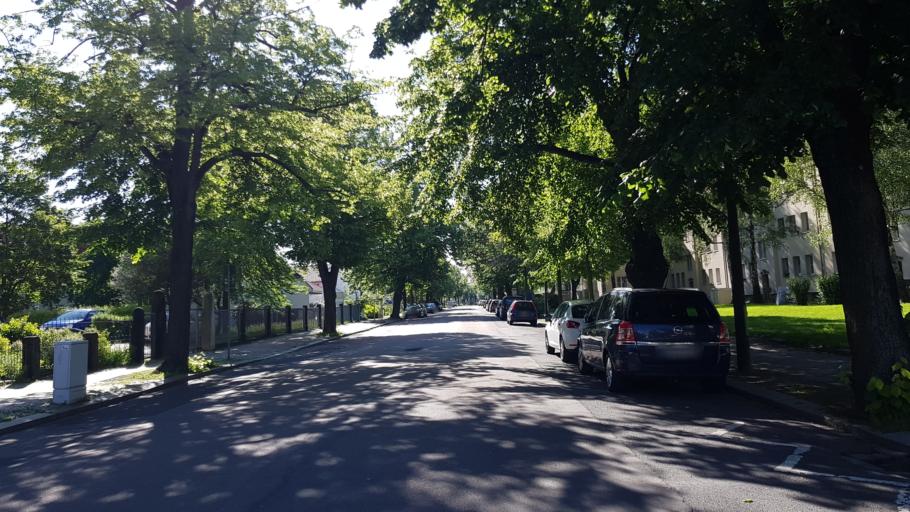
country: DE
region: Saxony
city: Heidenau
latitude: 51.0102
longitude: 13.8250
